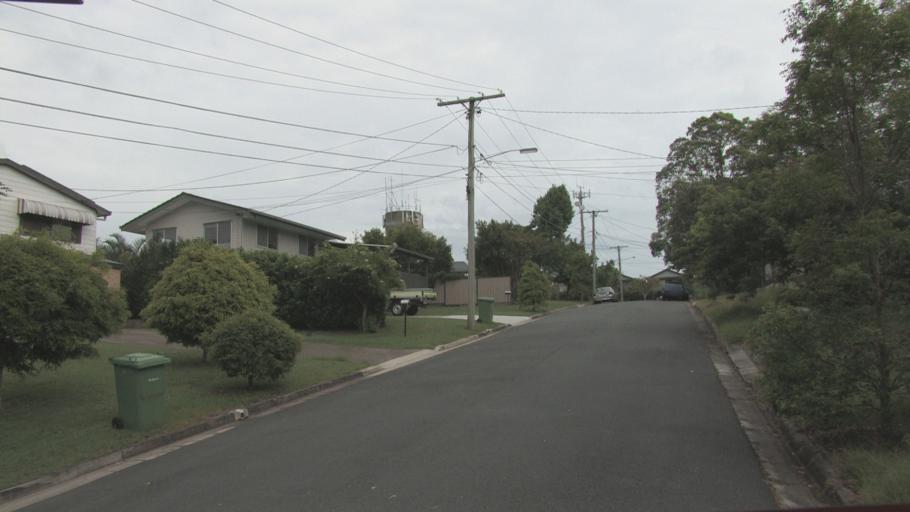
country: AU
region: Queensland
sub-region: Logan
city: Springwood
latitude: -27.6237
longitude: 153.1484
